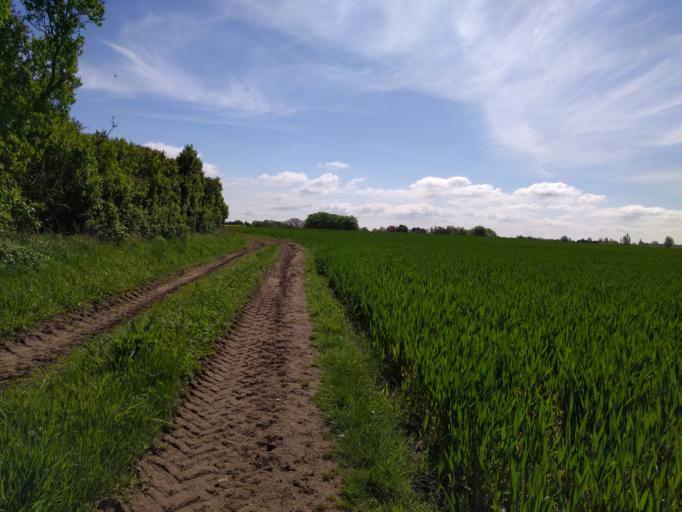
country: DK
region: South Denmark
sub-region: Kerteminde Kommune
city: Langeskov
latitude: 55.3842
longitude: 10.5552
